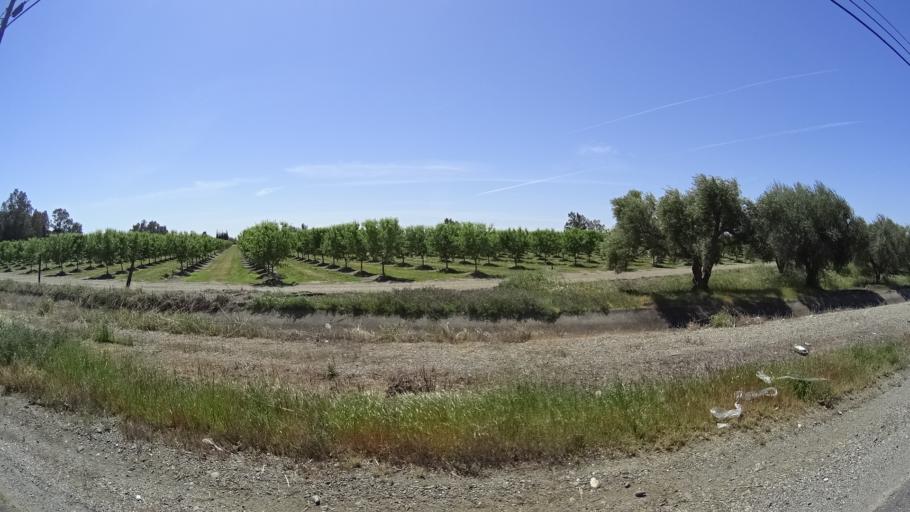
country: US
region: California
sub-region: Glenn County
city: Orland
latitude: 39.7349
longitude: -122.1654
